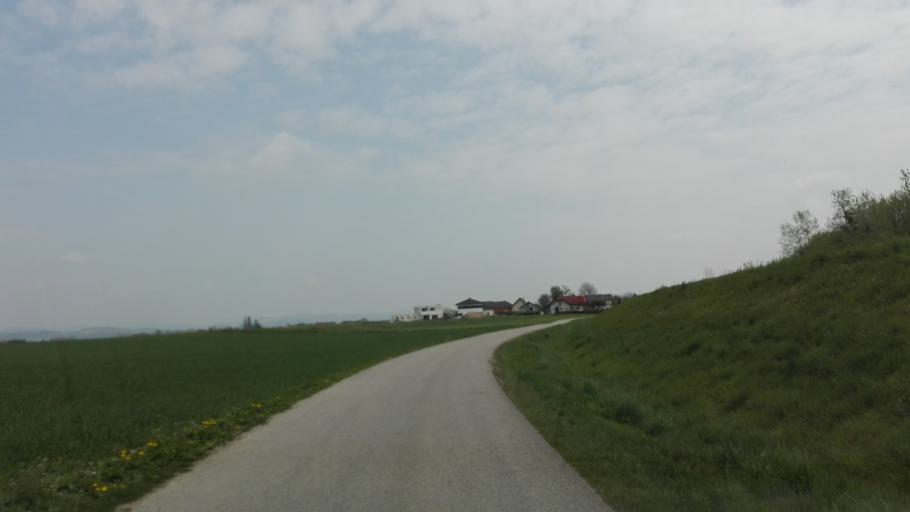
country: AT
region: Lower Austria
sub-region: Politischer Bezirk Amstetten
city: Strengberg
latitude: 48.1820
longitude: 14.6611
